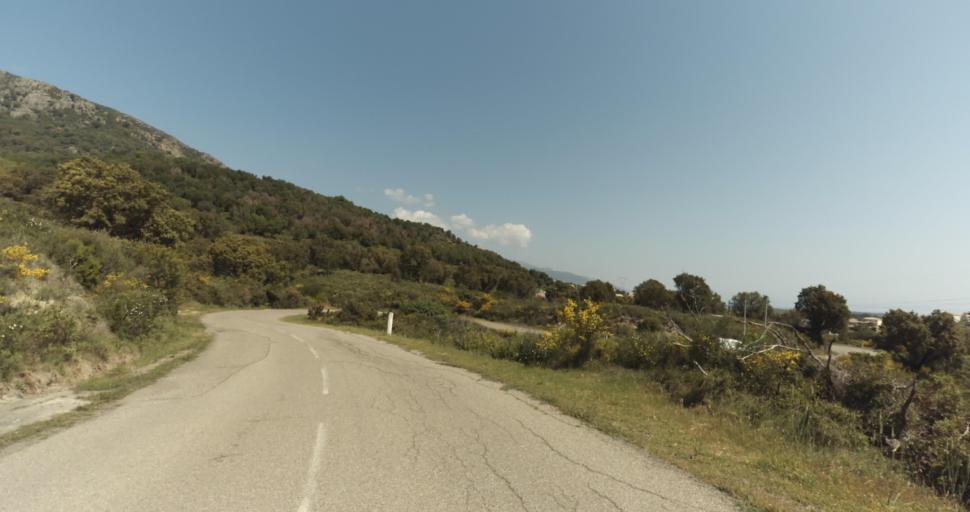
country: FR
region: Corsica
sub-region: Departement de la Haute-Corse
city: Biguglia
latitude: 42.6154
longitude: 9.4228
